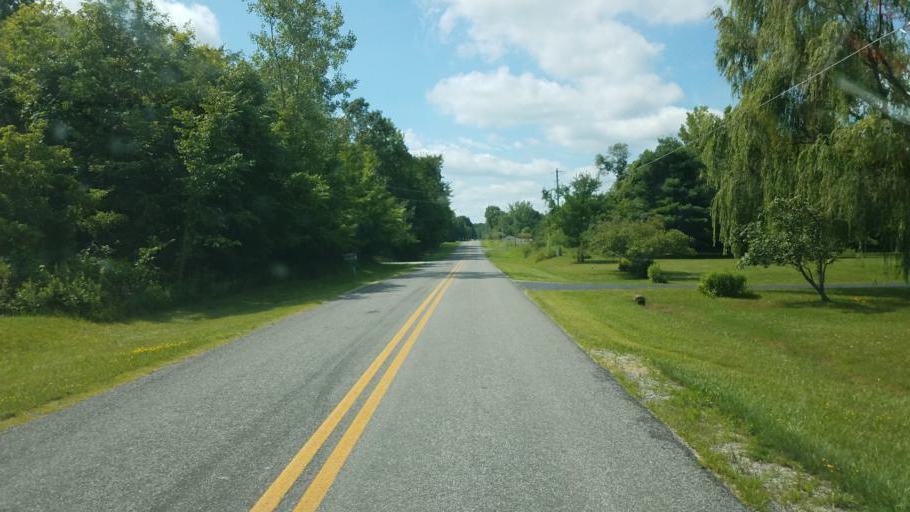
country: US
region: Ohio
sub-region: Delaware County
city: Sunbury
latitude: 40.2969
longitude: -82.9447
